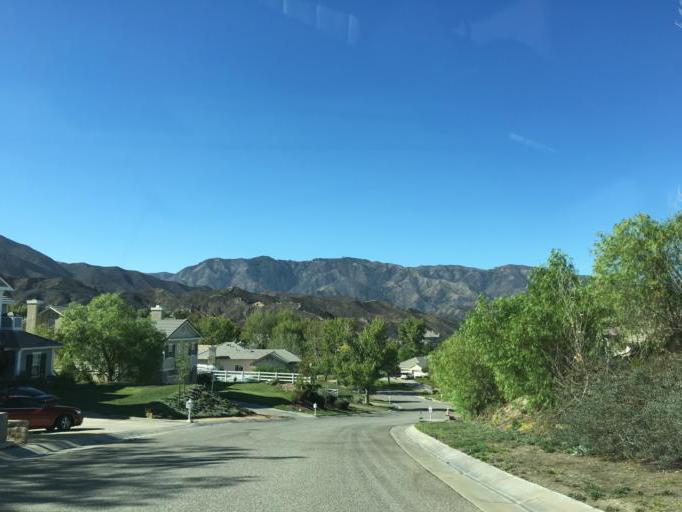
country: US
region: California
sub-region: Los Angeles County
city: Agua Dulce
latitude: 34.4027
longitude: -118.4021
